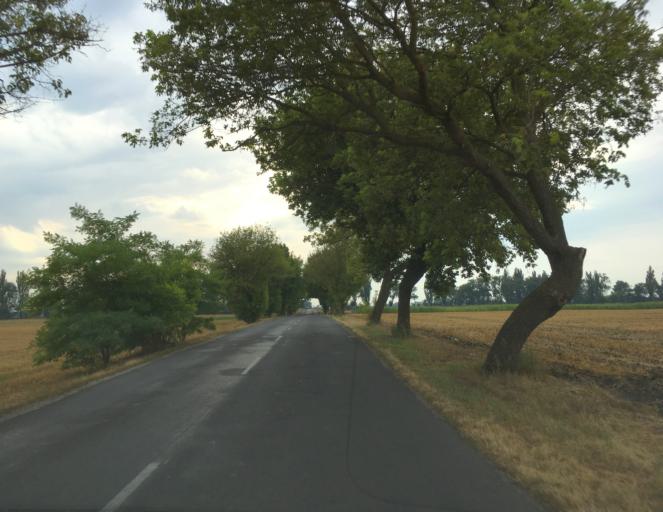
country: SK
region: Trnavsky
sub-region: Okres Dunajska Streda
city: Velky Meder
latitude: 47.9069
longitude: 17.7779
